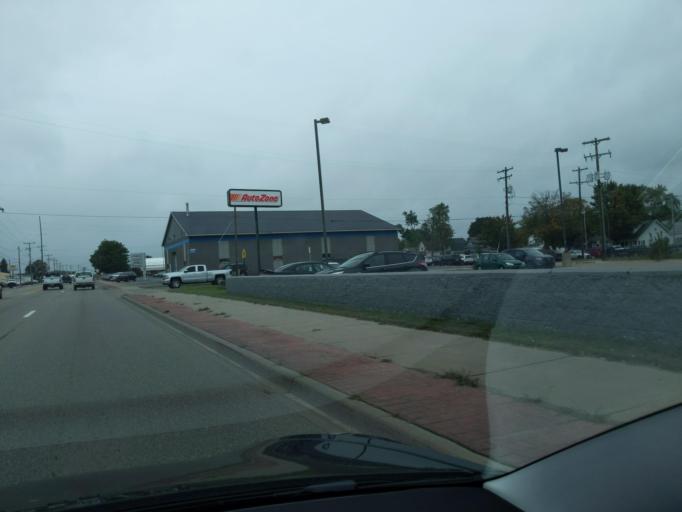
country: US
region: Michigan
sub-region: Wexford County
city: Cadillac
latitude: 44.2628
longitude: -85.4057
